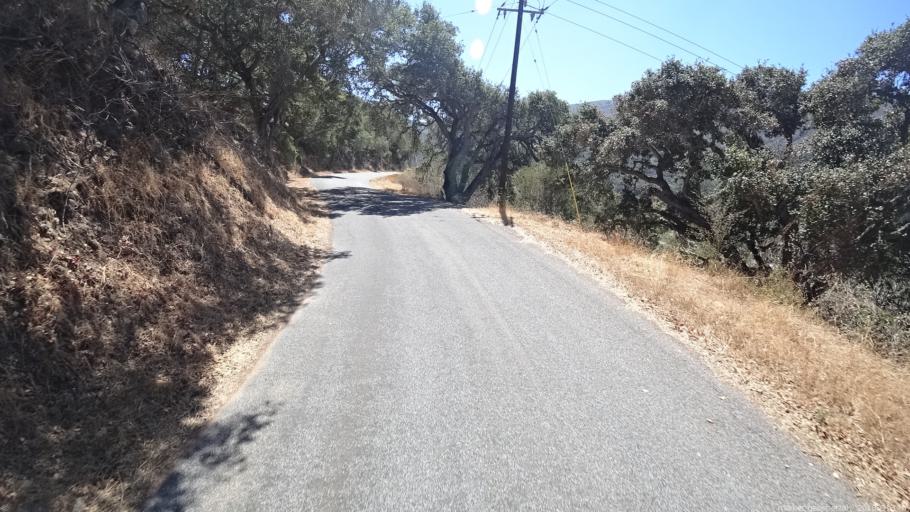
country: US
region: California
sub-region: Monterey County
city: Carmel Valley Village
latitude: 36.5128
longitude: -121.7694
